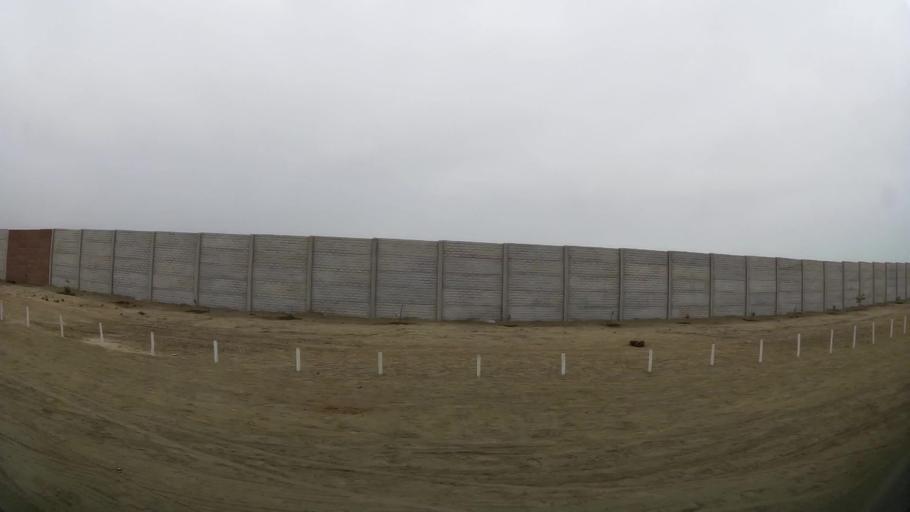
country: PE
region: Lima
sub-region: Lima
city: Punta Hermosa
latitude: -12.3262
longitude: -76.8333
